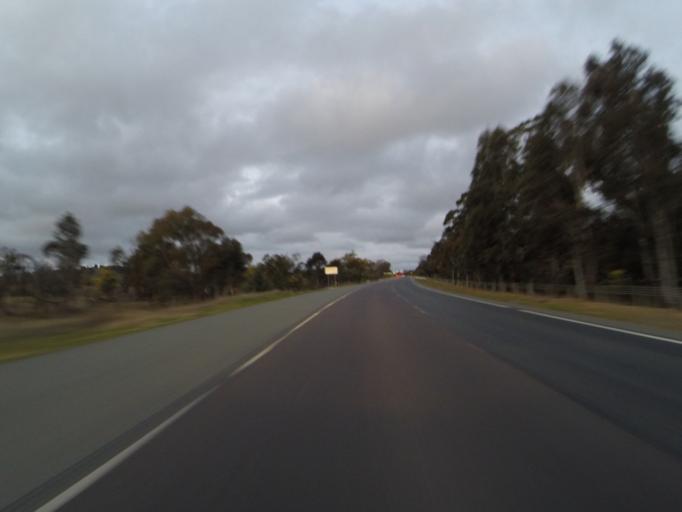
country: AU
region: Australian Capital Territory
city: Kaleen
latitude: -35.2062
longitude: 149.1958
